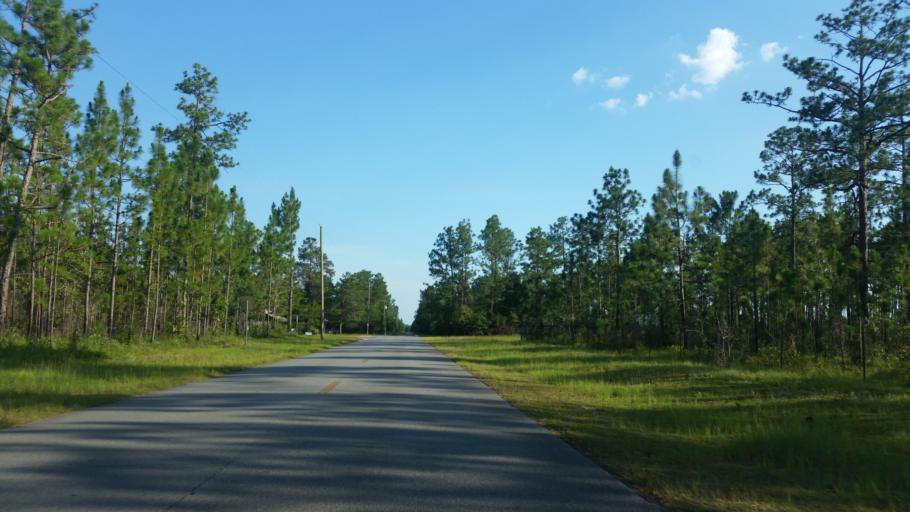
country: US
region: Florida
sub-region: Santa Rosa County
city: East Milton
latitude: 30.6870
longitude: -86.8763
